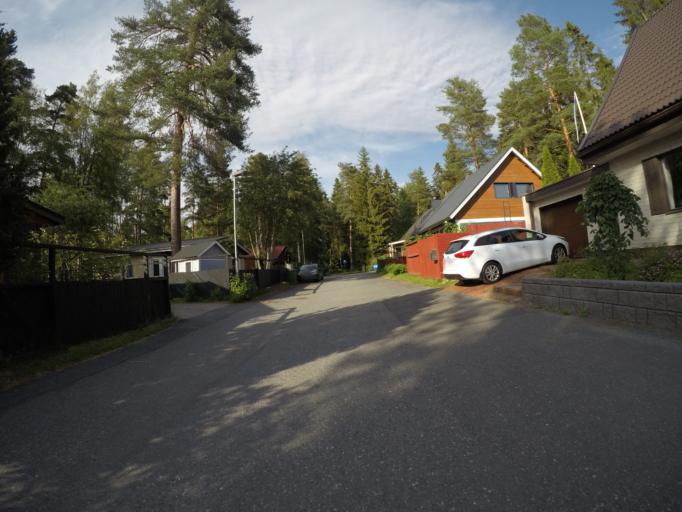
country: FI
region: Haeme
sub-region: Haemeenlinna
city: Haemeenlinna
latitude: 60.9755
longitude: 24.3914
